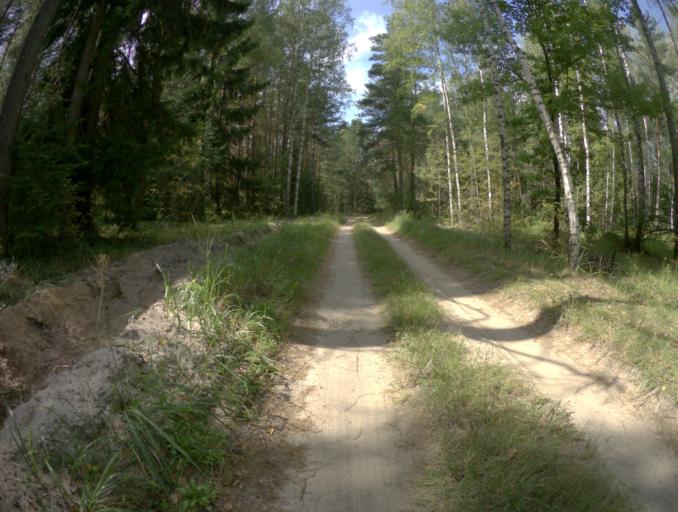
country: RU
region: Vladimir
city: Vorsha
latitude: 55.9630
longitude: 40.1946
